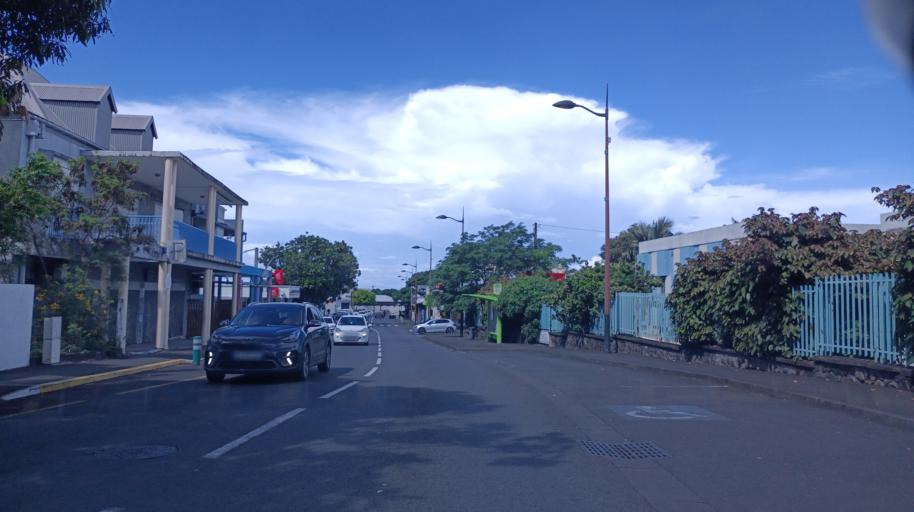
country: RE
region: Reunion
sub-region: Reunion
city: Saint-Joseph
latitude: -21.3788
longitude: 55.6153
